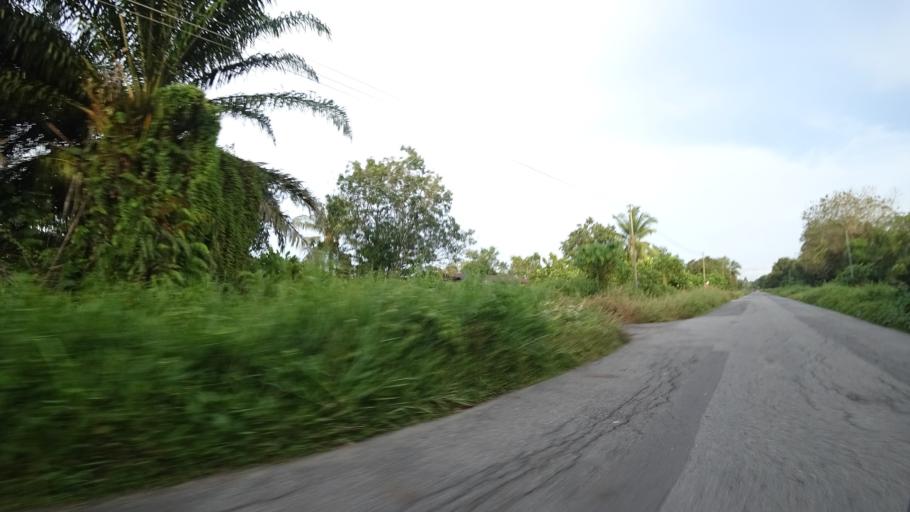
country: BN
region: Tutong
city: Tutong
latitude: 4.8173
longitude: 114.8194
